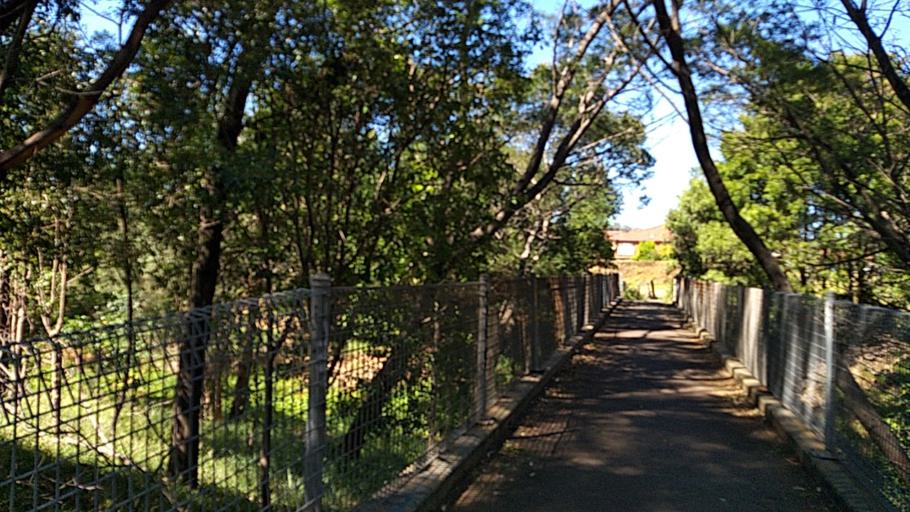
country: AU
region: New South Wales
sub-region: Wollongong
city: Fairy Meadow
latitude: -34.3919
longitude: 150.8884
